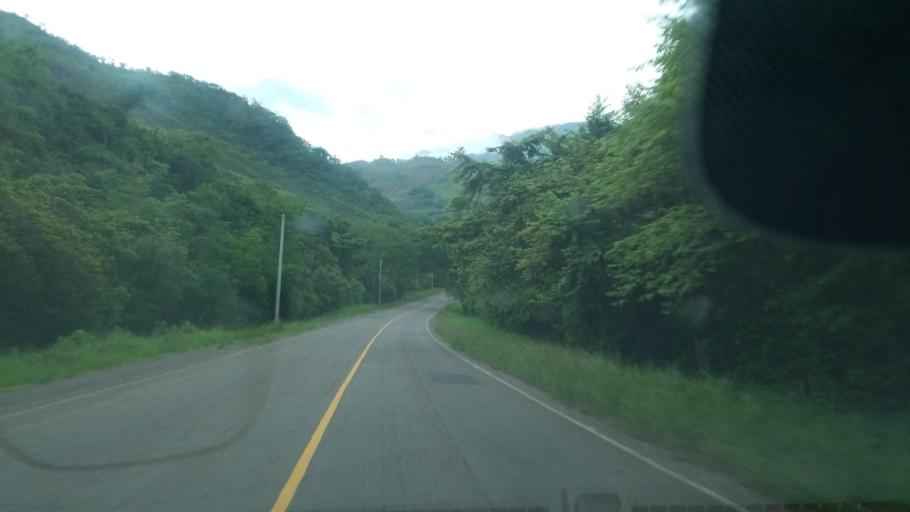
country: HN
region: Santa Barbara
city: Ceguaca
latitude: 14.8099
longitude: -88.1852
